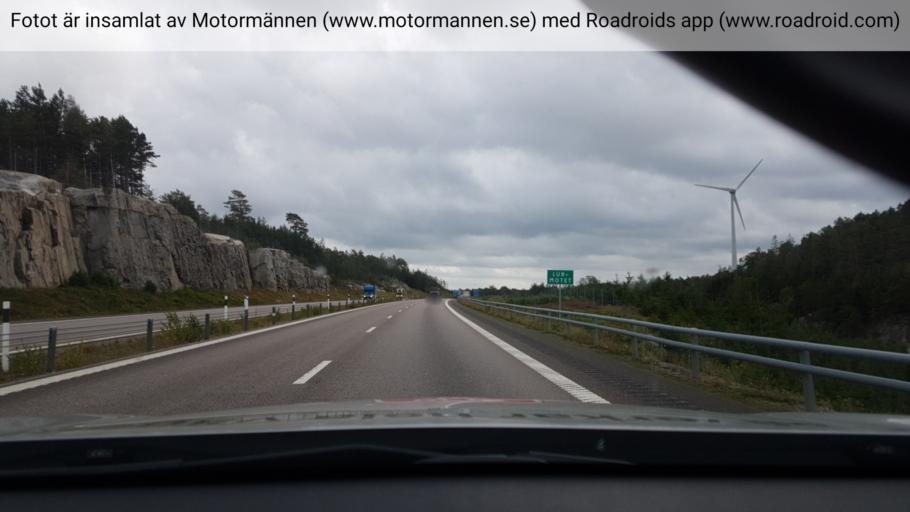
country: SE
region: Vaestra Goetaland
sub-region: Tanums Kommun
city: Tanumshede
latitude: 58.8258
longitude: 11.2811
